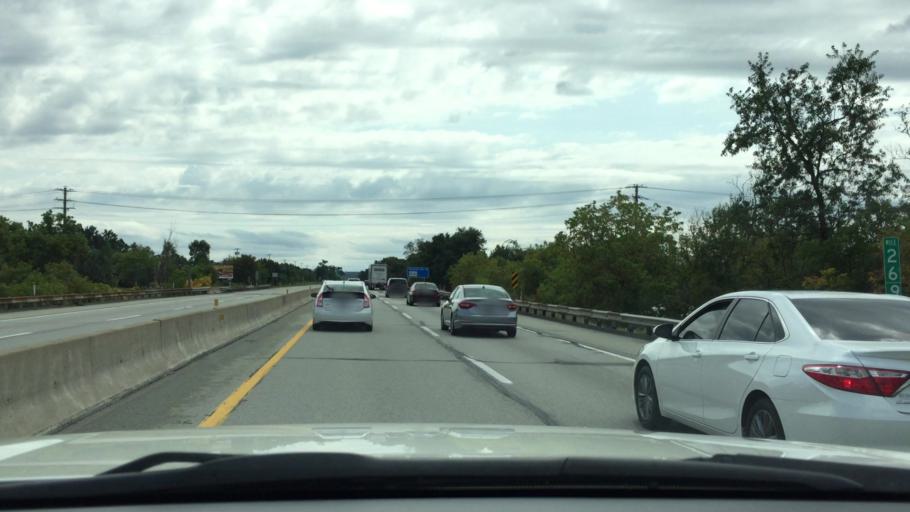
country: US
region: Pennsylvania
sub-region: Butler County
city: Fernway
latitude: 40.6991
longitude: -80.1181
